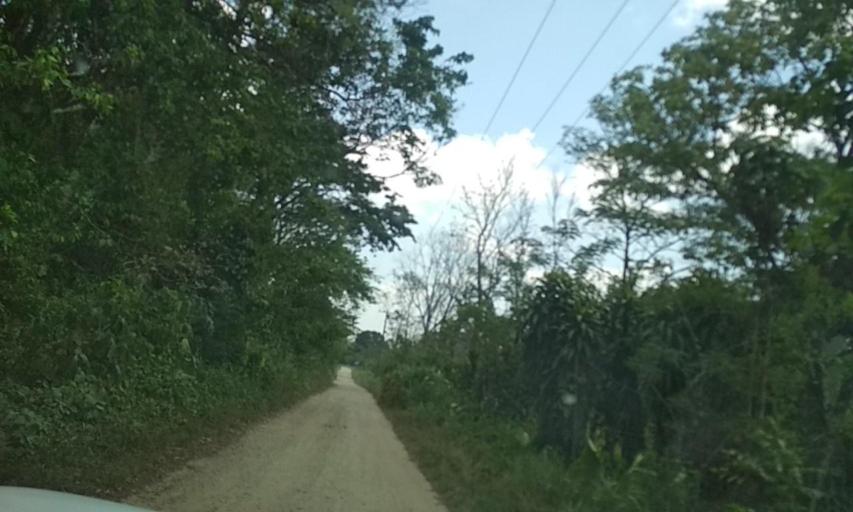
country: MX
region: Chiapas
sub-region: Tecpatan
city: Raudales Malpaso
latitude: 17.2855
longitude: -93.8379
